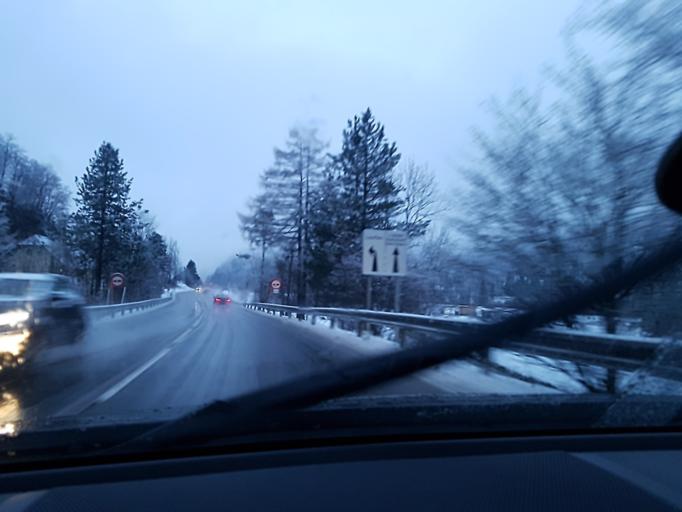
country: AT
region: Upper Austria
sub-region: Politischer Bezirk Gmunden
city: Bad Goisern
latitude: 47.6695
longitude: 13.6105
